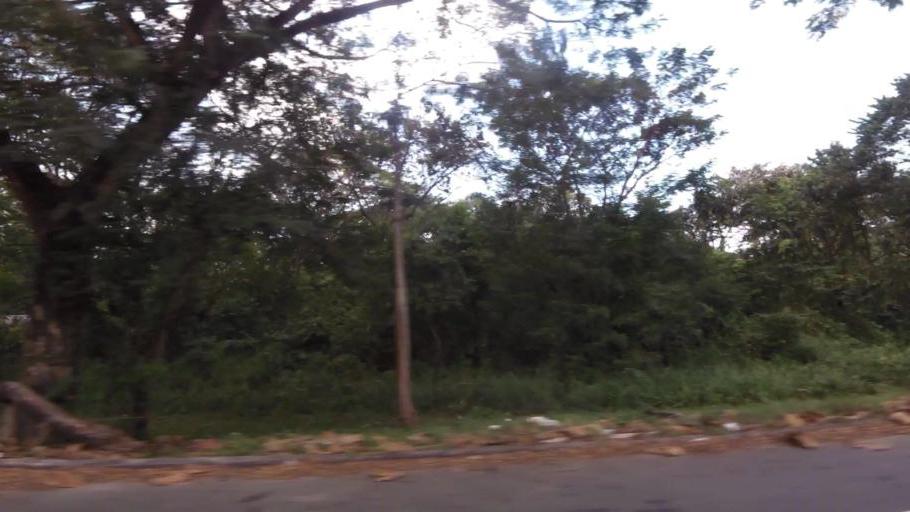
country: CO
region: Bolivar
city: Turbaco
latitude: 10.3702
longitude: -75.4533
